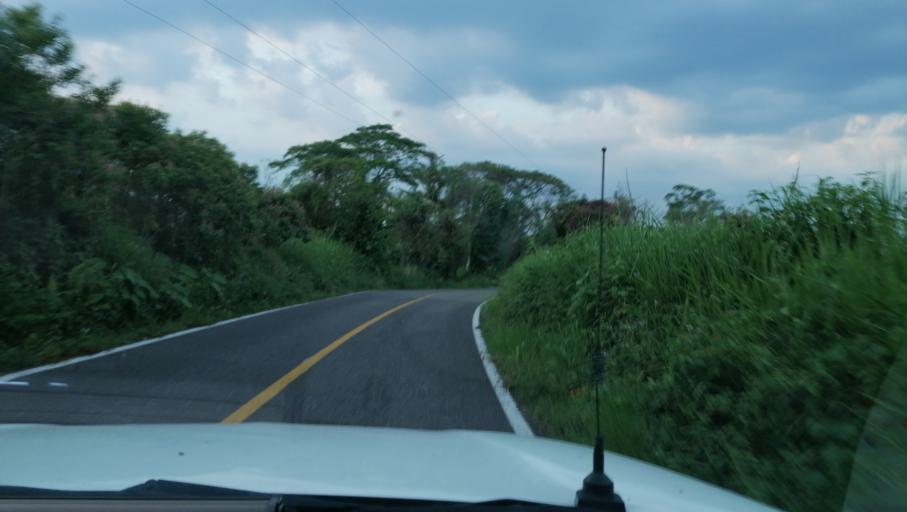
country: MX
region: Chiapas
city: Pichucalco
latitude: 17.5158
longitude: -93.1557
